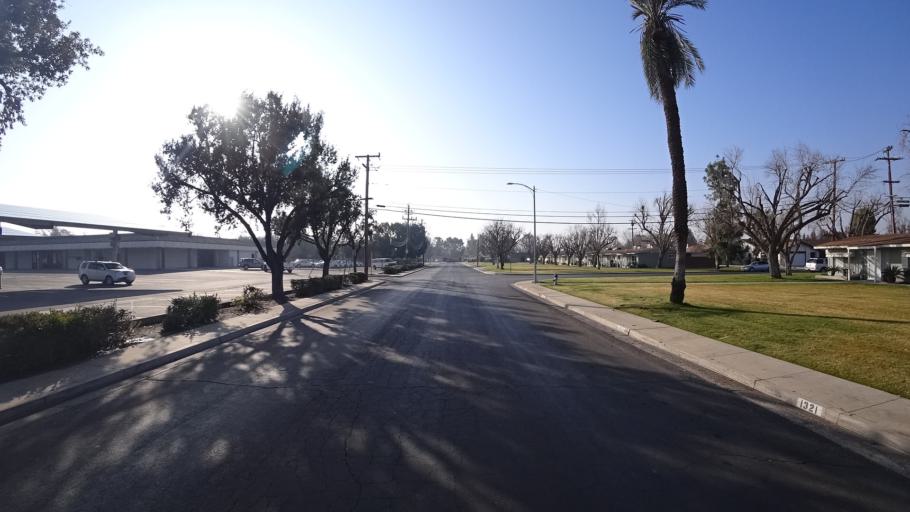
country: US
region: California
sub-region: Kern County
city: Bakersfield
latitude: 35.3429
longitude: -119.0662
